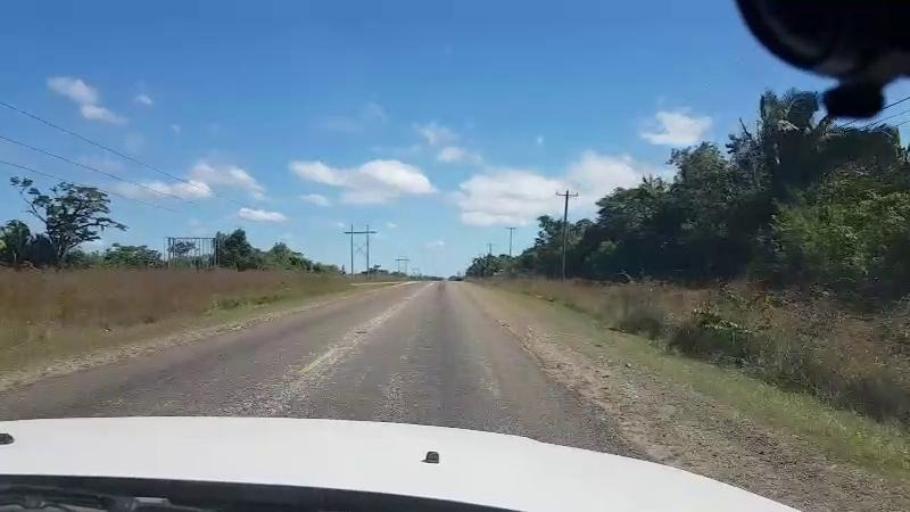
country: BZ
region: Cayo
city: Belmopan
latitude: 17.2768
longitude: -88.7325
